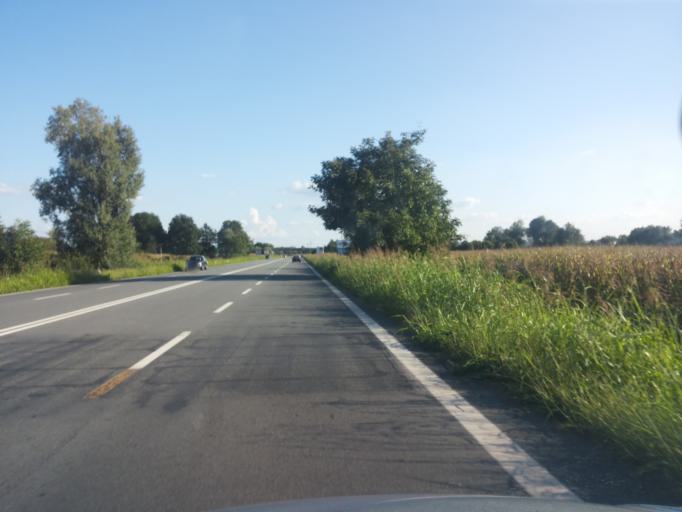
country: IT
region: Piedmont
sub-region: Provincia di Torino
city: Ivrea
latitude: 45.4394
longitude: 7.8835
